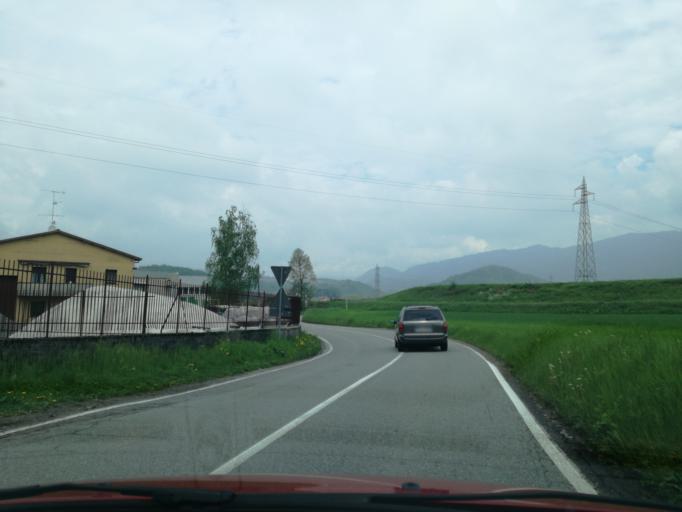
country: IT
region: Lombardy
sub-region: Provincia di Lecco
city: Canova-San Zeno
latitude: 45.7112
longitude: 9.4042
